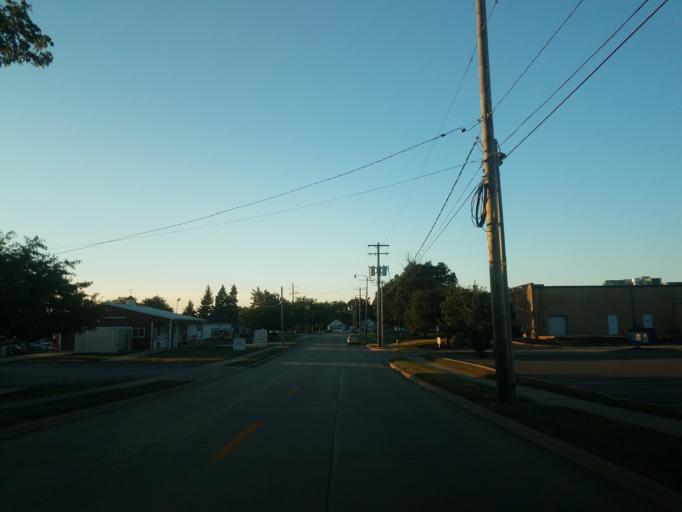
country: US
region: Illinois
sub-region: McLean County
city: Bloomington
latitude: 40.4809
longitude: -89.0159
